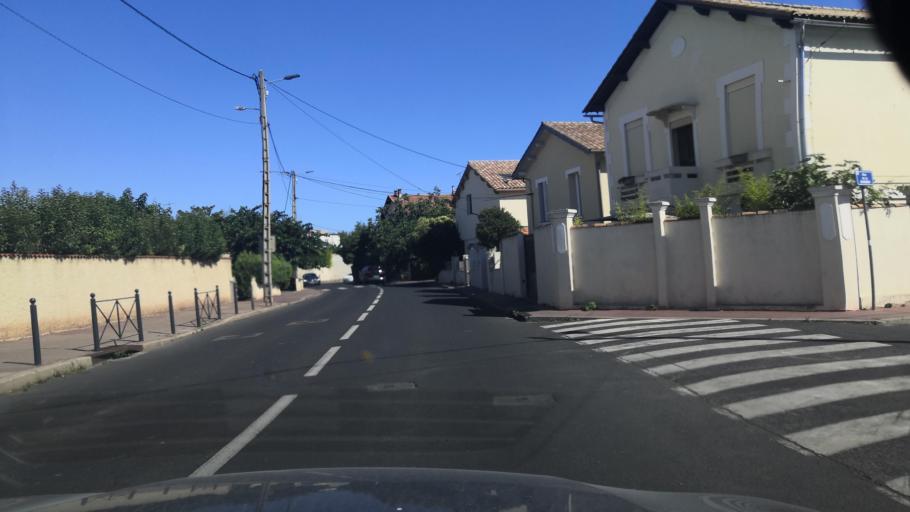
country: FR
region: Languedoc-Roussillon
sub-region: Departement de l'Herault
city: Montpellier
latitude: 43.5922
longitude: 3.8878
